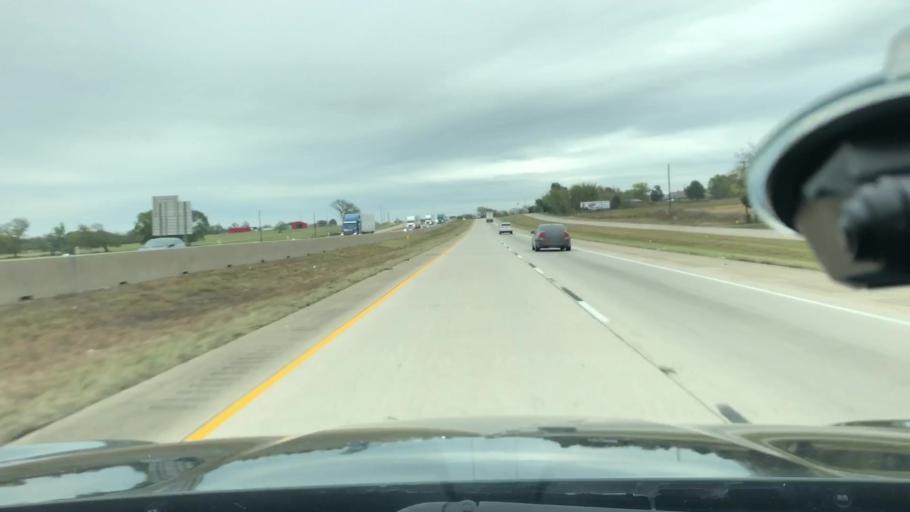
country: US
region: Texas
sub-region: Hopkins County
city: Sulphur Springs
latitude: 33.1219
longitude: -95.7297
